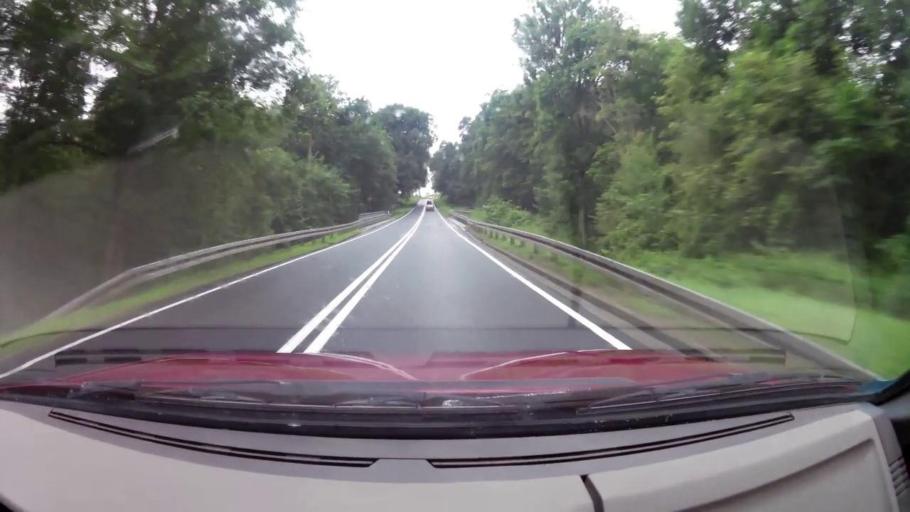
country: PL
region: West Pomeranian Voivodeship
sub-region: Powiat stargardzki
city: Marianowo
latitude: 53.4088
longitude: 15.2289
